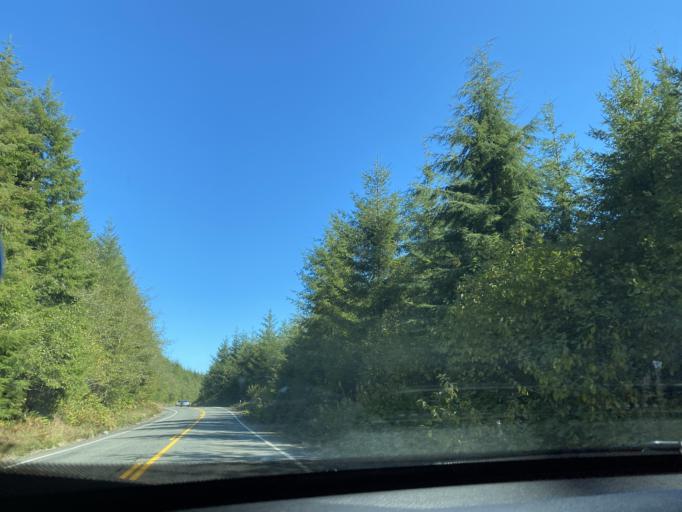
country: US
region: Washington
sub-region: Clallam County
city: Forks
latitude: 47.9324
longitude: -124.4786
